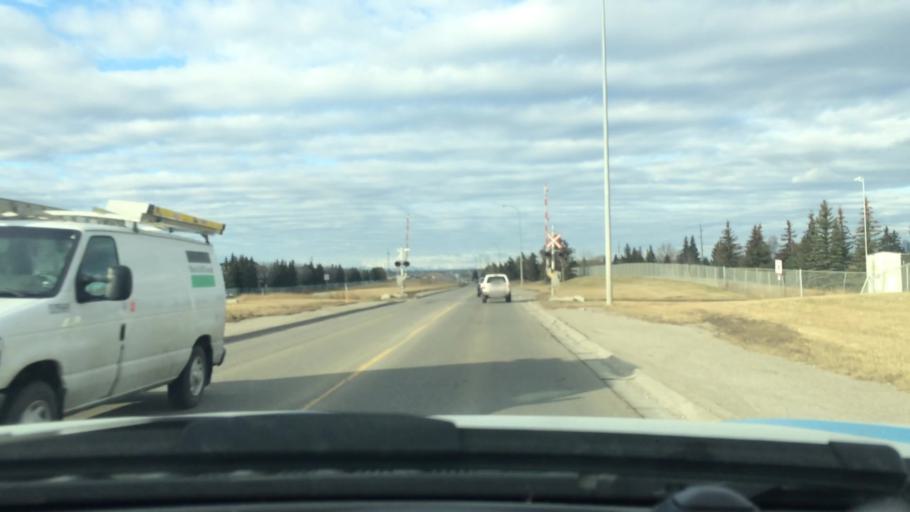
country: CA
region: Alberta
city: Calgary
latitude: 51.0153
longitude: -113.9849
